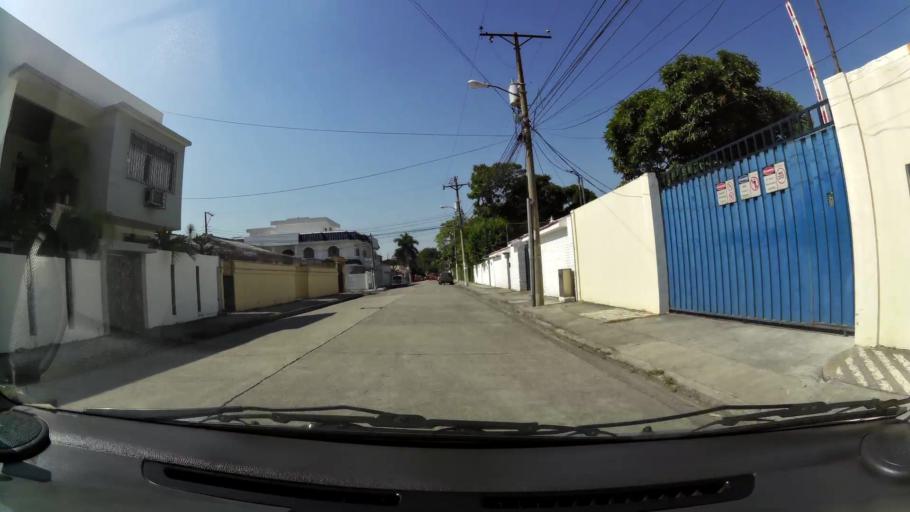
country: EC
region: Guayas
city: Guayaquil
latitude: -2.1680
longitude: -79.9186
